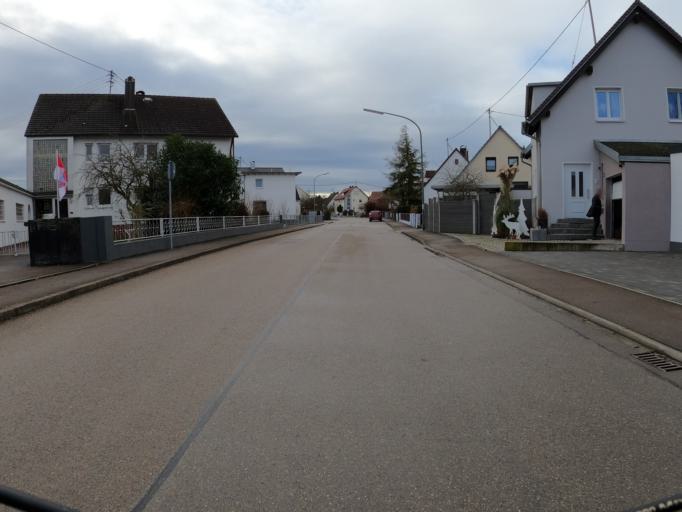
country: DE
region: Bavaria
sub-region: Swabia
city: Holzheim
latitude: 48.4090
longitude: 10.0687
